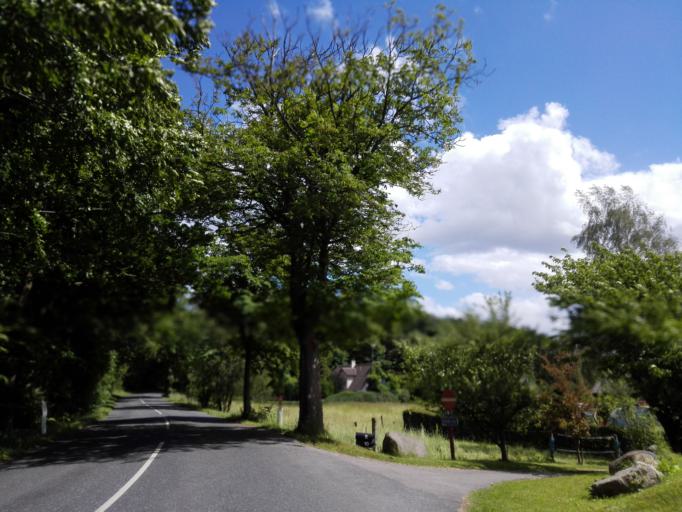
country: DK
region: Capital Region
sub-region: Allerod Kommune
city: Lynge
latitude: 55.8219
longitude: 12.3028
